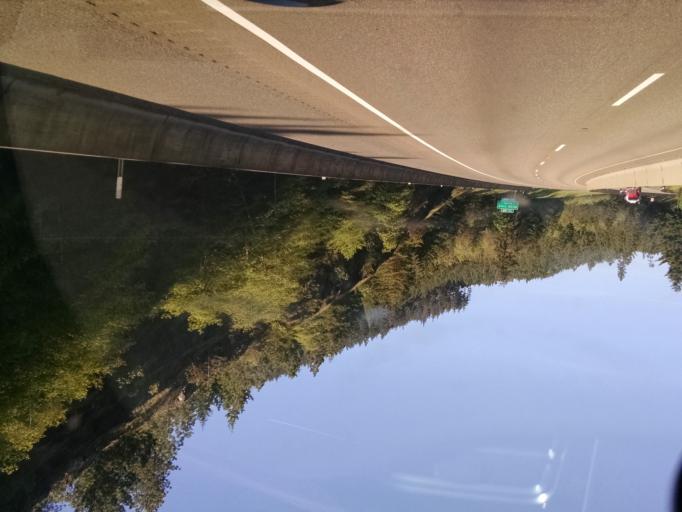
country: US
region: Oregon
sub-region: Douglas County
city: Myrtle Creek
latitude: 43.0298
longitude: -123.3161
